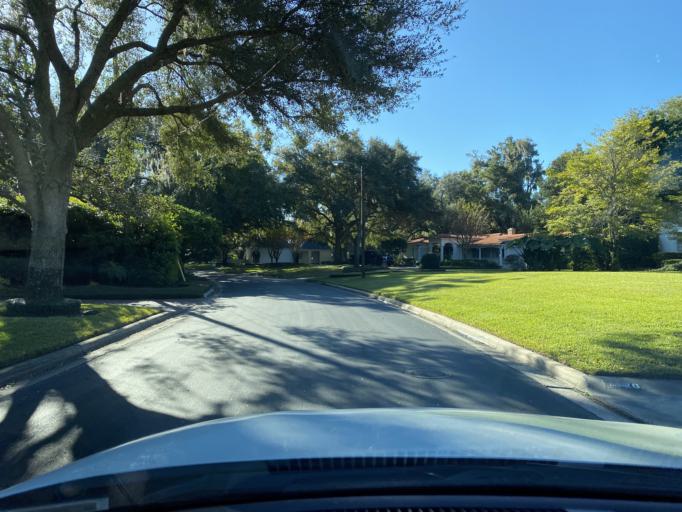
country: US
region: Florida
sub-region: Orange County
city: Orlando
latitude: 28.5557
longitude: -81.4021
